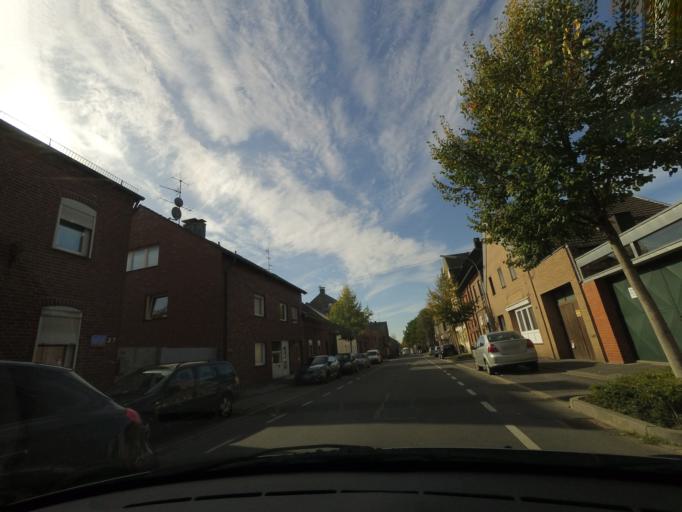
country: DE
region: North Rhine-Westphalia
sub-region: Regierungsbezirk Dusseldorf
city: Neubrueck
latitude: 51.1673
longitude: 6.5797
